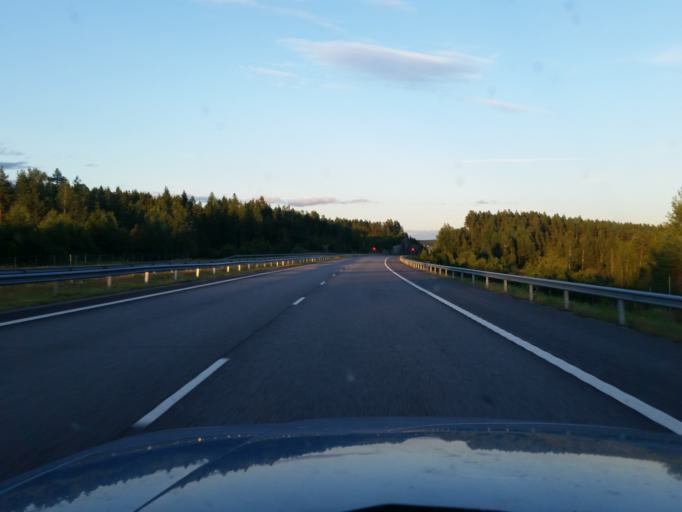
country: FI
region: Varsinais-Suomi
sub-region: Salo
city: Halikko
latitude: 60.4341
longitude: 22.9799
